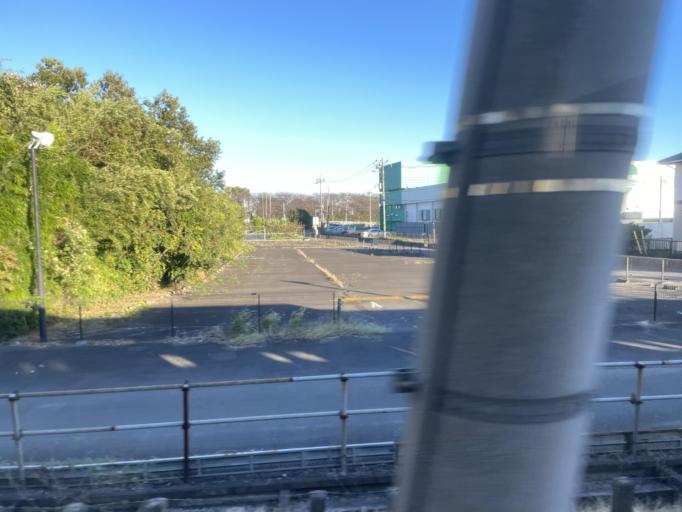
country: JP
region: Saitama
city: Satte
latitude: 36.0949
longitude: 139.7189
